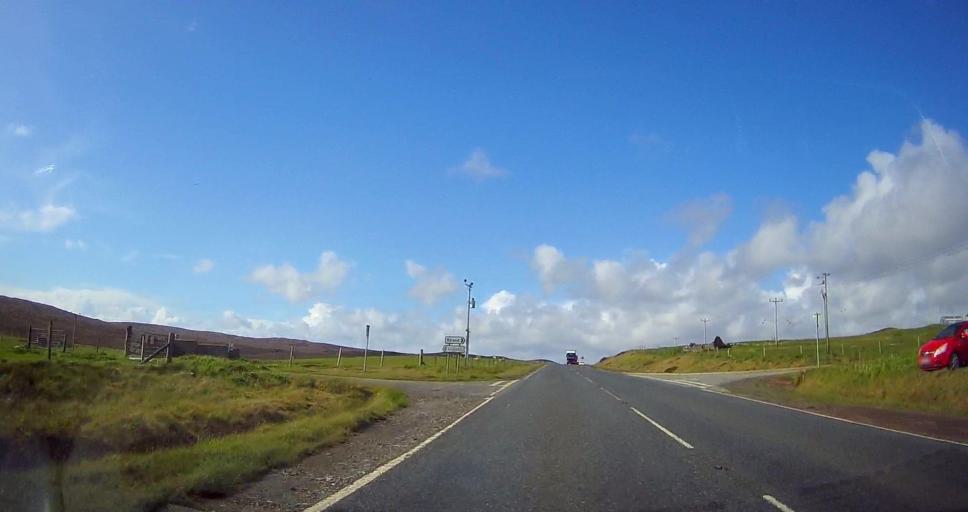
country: GB
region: Scotland
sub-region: Shetland Islands
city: Lerwick
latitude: 60.1981
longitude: -1.2322
